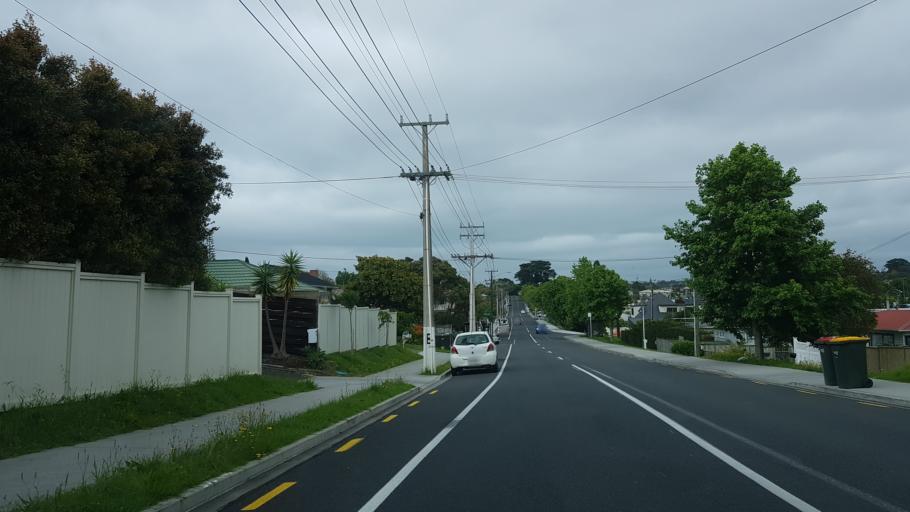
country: NZ
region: Auckland
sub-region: Auckland
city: North Shore
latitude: -36.8001
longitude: 174.7493
